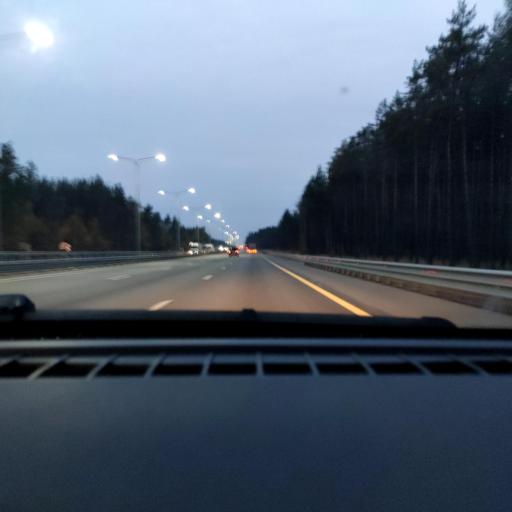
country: RU
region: Voronezj
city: Somovo
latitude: 51.7179
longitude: 39.3085
